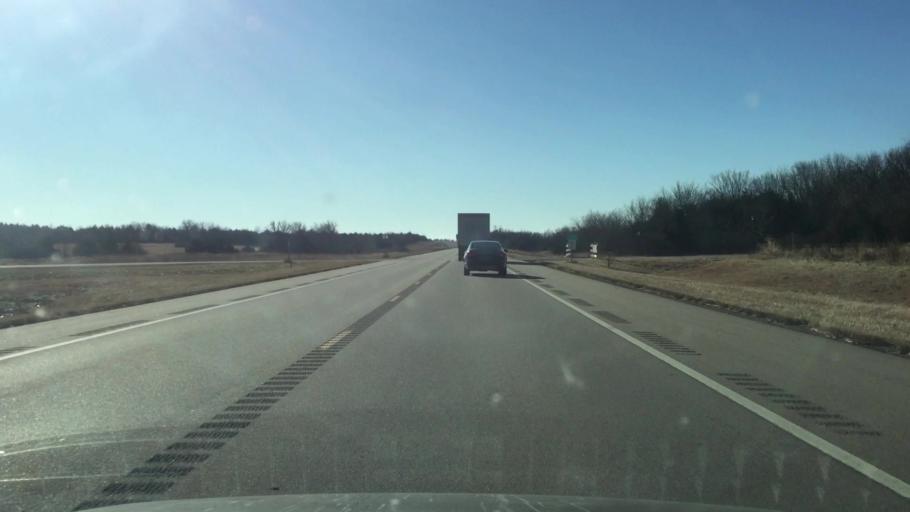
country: US
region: Kansas
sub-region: Allen County
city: Iola
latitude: 38.0392
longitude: -95.3806
